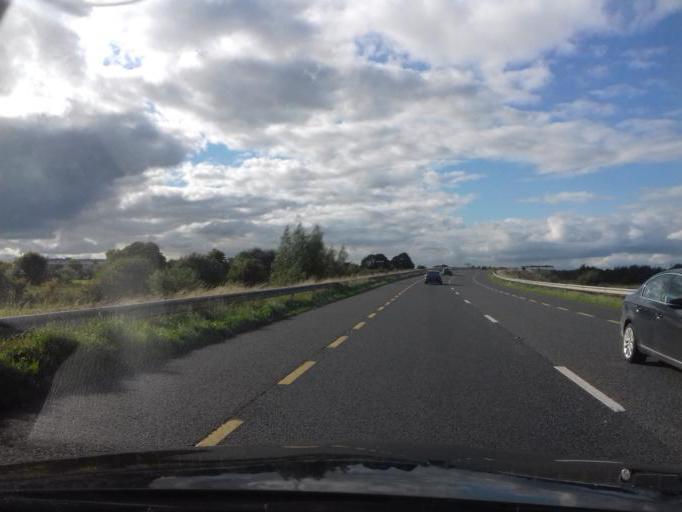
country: IE
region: Leinster
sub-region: Uibh Fhaili
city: Tullamore
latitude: 53.2832
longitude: -7.4746
